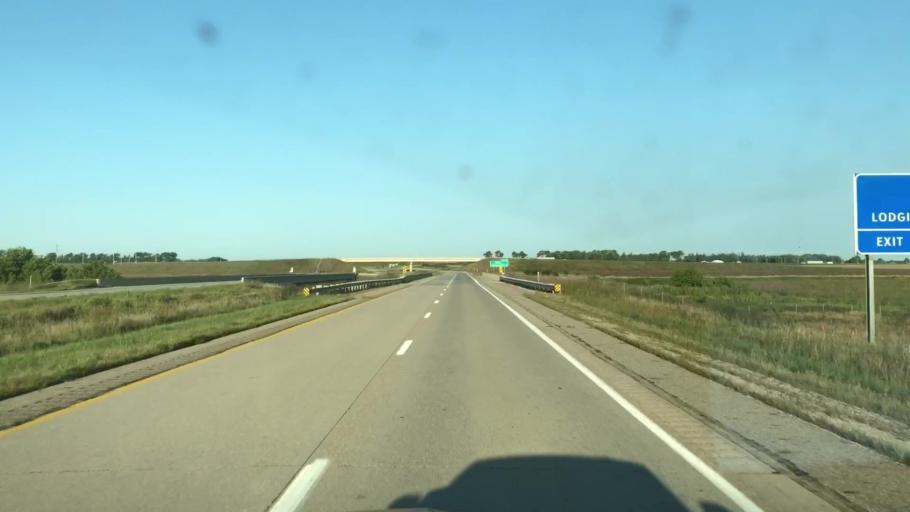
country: US
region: Iowa
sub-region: Osceola County
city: Sibley
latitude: 43.3845
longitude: -95.7356
